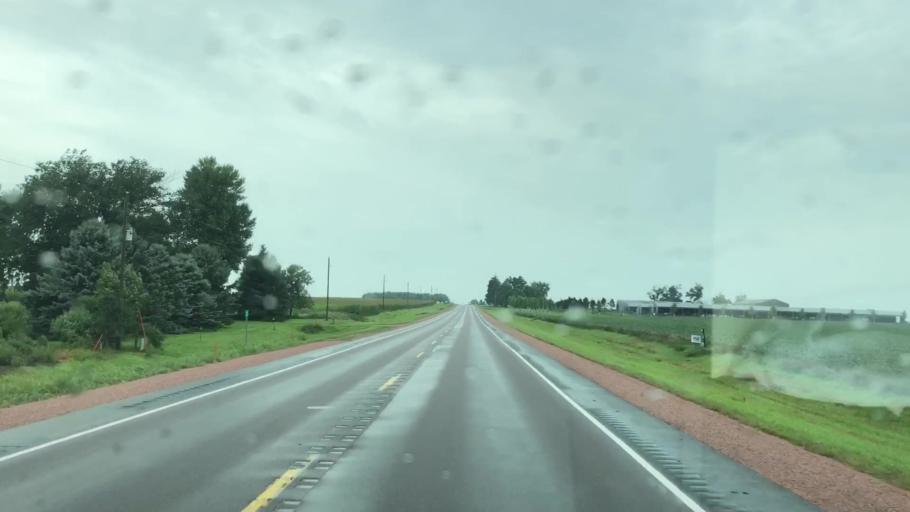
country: US
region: Iowa
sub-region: O'Brien County
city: Sheldon
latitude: 43.1860
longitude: -95.7755
